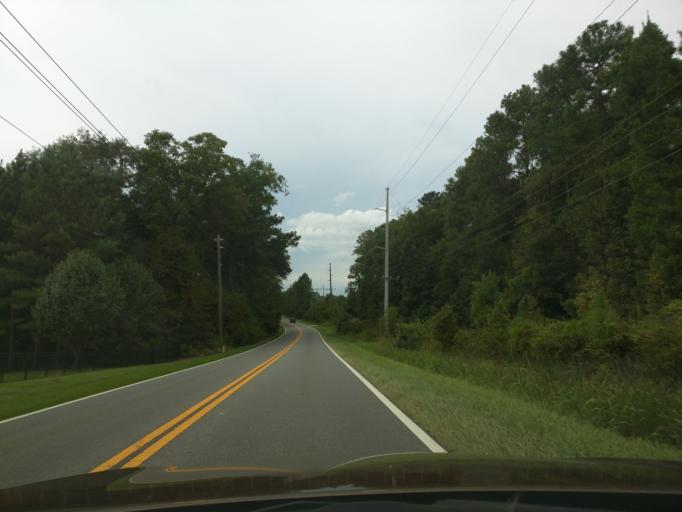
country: US
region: Florida
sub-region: Leon County
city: Tallahassee
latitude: 30.5821
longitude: -84.2424
